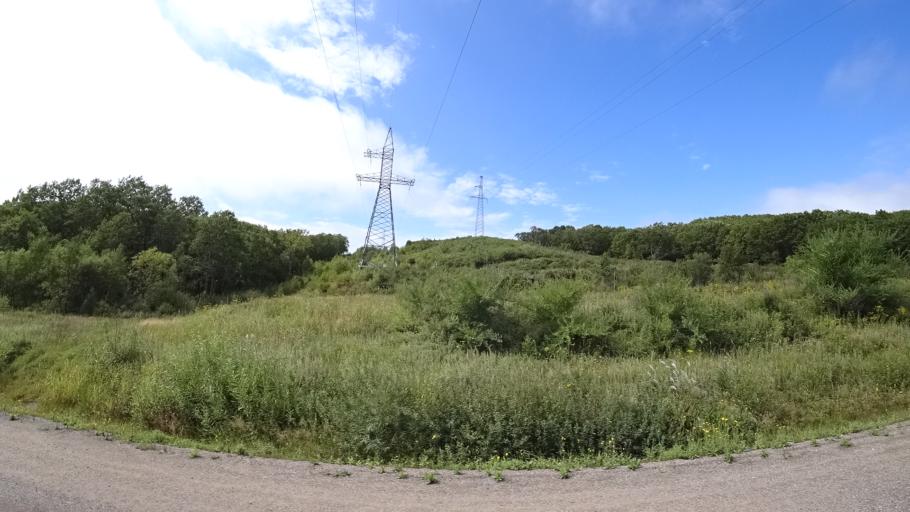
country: RU
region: Primorskiy
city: Lyalichi
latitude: 44.1216
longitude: 132.4207
